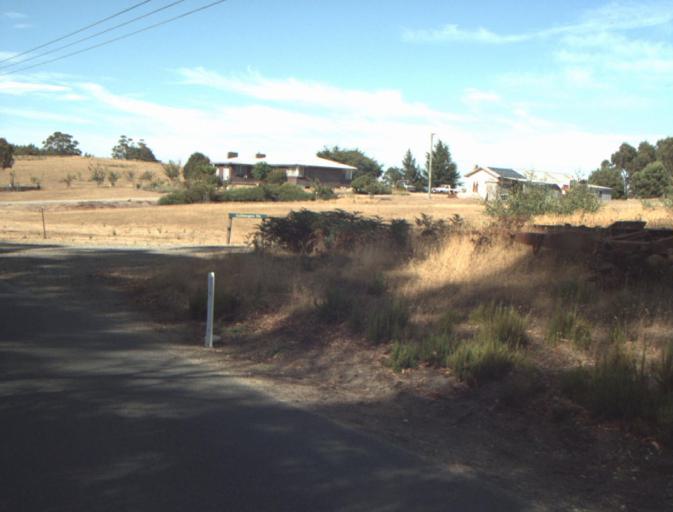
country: AU
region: Tasmania
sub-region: Launceston
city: Mayfield
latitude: -41.2063
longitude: 147.2150
